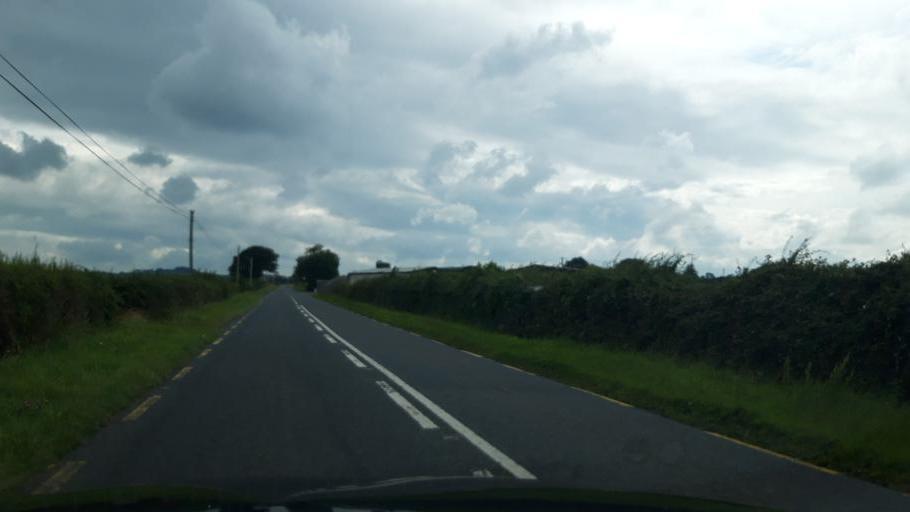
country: IE
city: Ballylinan
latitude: 52.9217
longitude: -7.0631
